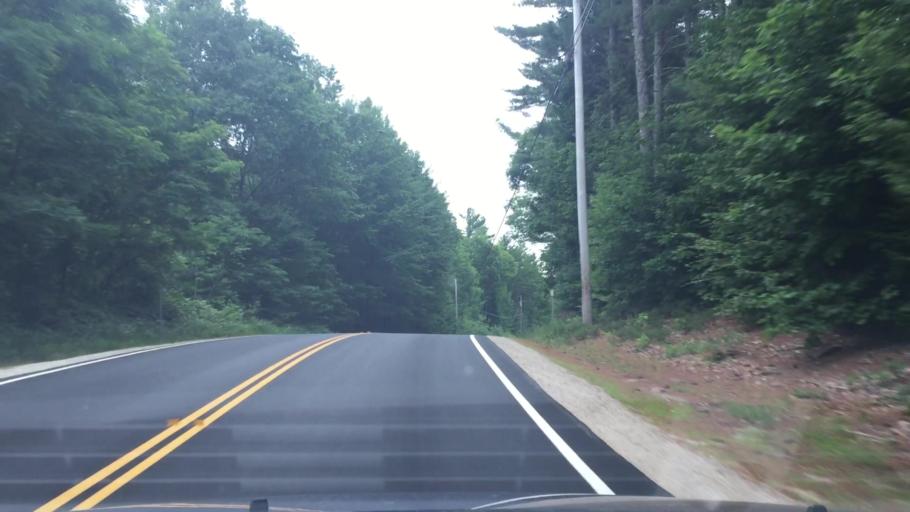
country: US
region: New Hampshire
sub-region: Carroll County
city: Freedom
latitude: 43.8373
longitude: -71.0787
